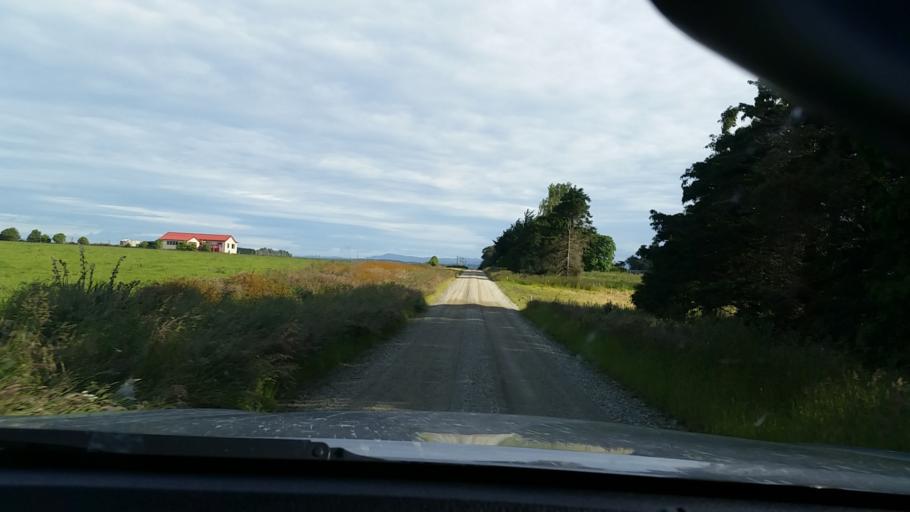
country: NZ
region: Southland
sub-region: Invercargill City
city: Invercargill
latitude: -46.2894
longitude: 168.6229
